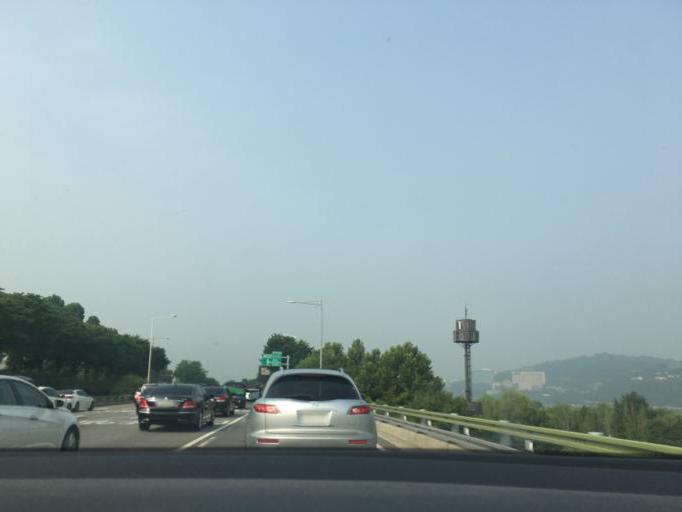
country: KR
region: Gyeonggi-do
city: Guri-si
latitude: 37.5628
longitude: 127.1299
